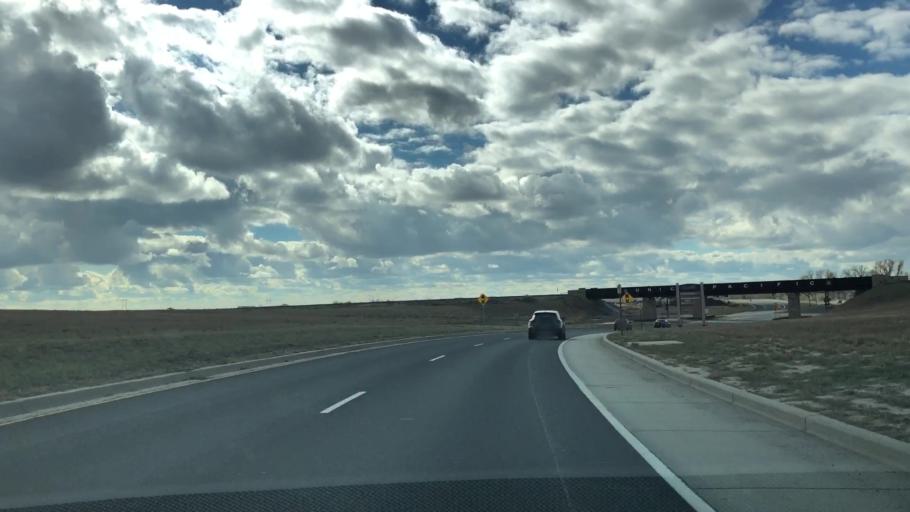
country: US
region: Colorado
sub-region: Larimer County
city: Loveland
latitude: 40.4183
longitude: -104.9836
